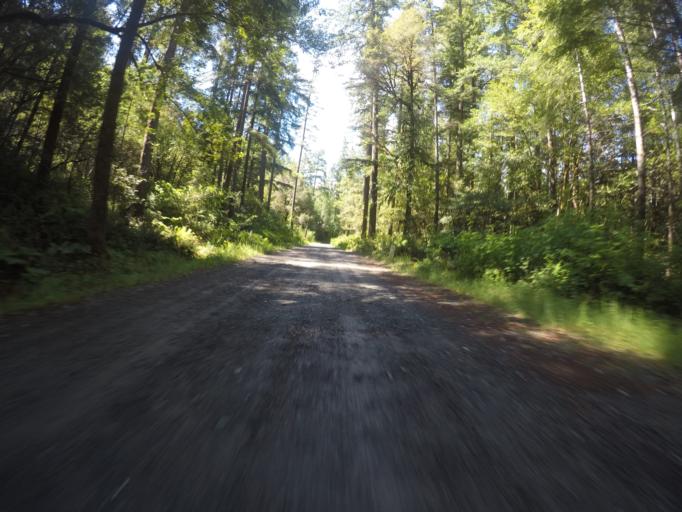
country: US
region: California
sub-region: Del Norte County
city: Bertsch-Oceanview
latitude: 41.6944
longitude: -123.9027
